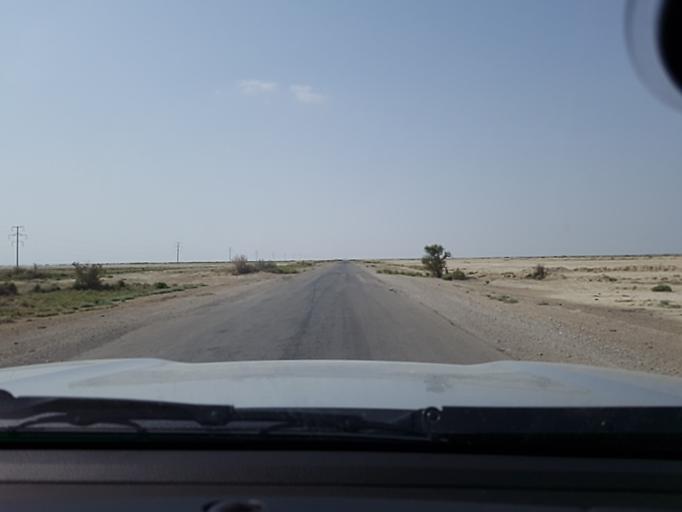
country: TM
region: Balkan
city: Gumdag
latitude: 38.9072
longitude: 54.5919
